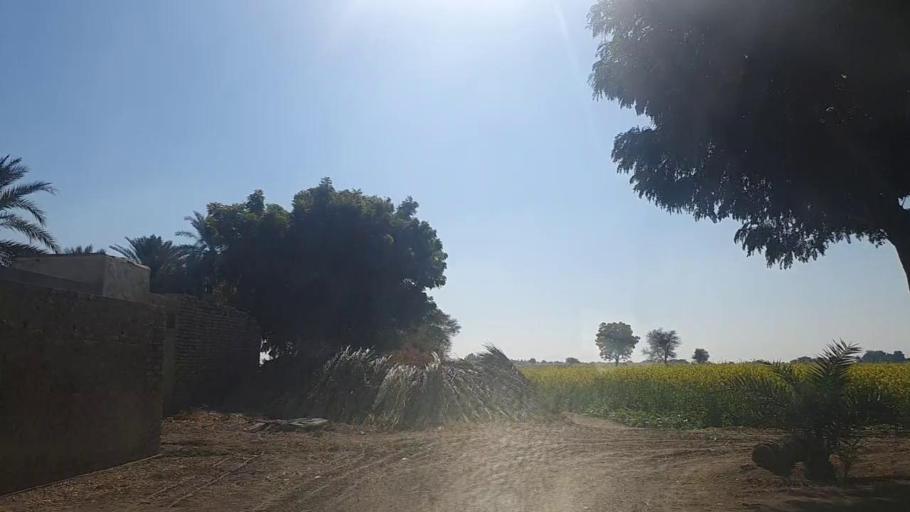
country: PK
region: Sindh
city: Sinjhoro
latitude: 26.1281
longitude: 68.8513
